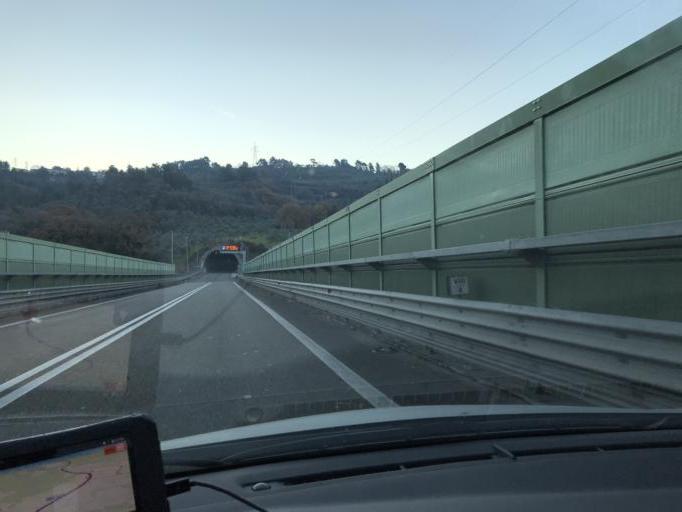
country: IT
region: Umbria
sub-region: Provincia di Terni
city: Terni
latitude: 42.5755
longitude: 12.6833
